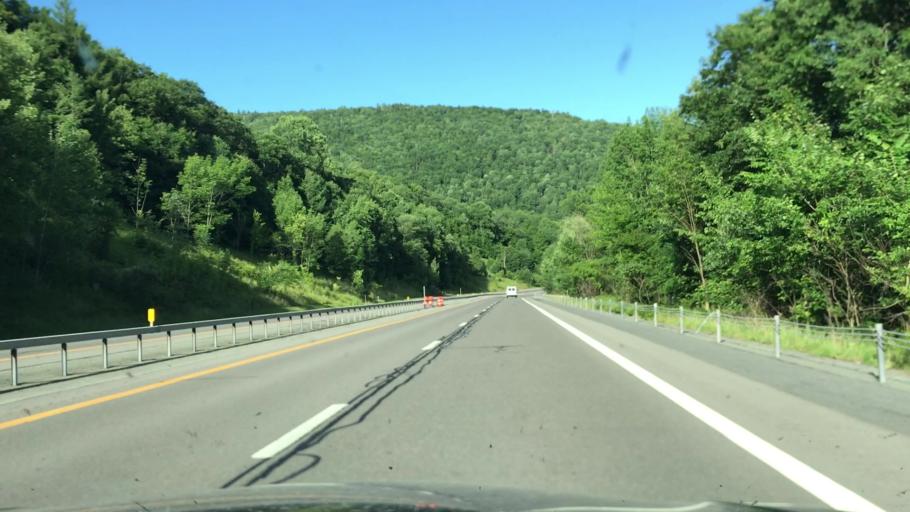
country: US
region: New York
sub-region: Delaware County
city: Hancock
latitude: 41.9757
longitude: -75.2031
